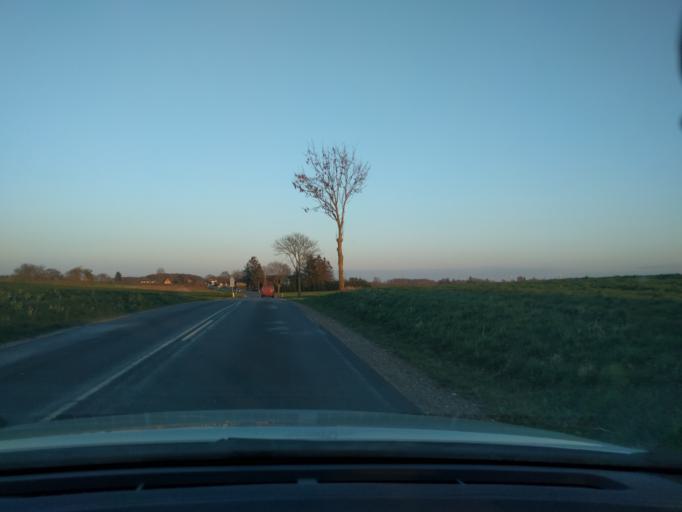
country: DK
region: South Denmark
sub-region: Assens Kommune
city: Glamsbjerg
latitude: 55.2712
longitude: 10.0651
